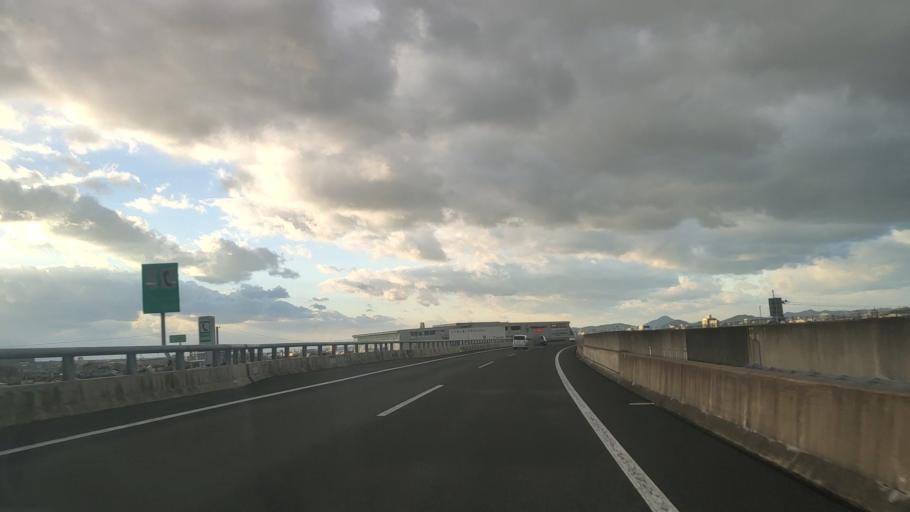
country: JP
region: Ehime
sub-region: Shikoku-chuo Shi
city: Matsuyama
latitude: 33.7884
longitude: 132.8076
